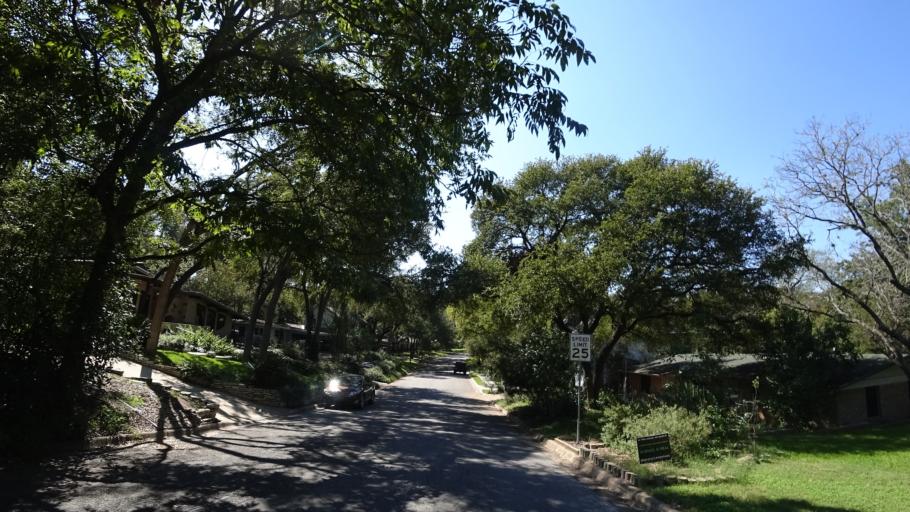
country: US
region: Texas
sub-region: Travis County
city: Rollingwood
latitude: 30.2464
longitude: -97.7848
